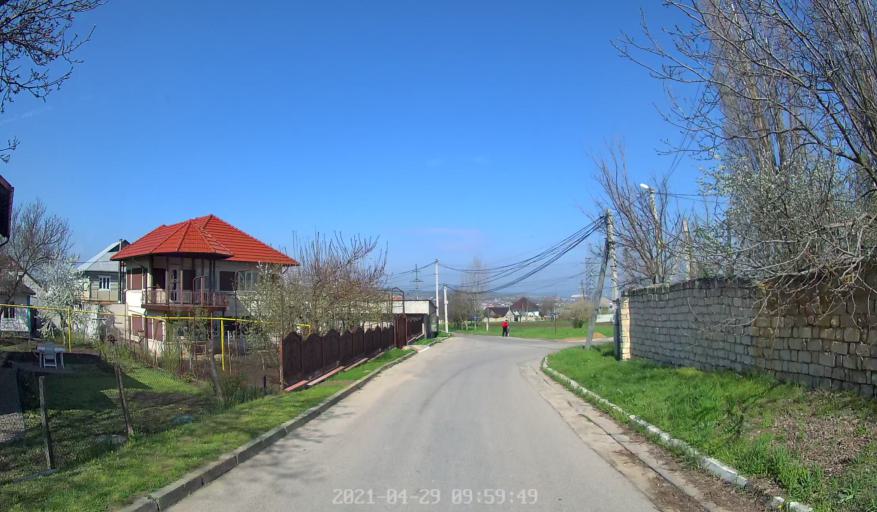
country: MD
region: Chisinau
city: Cricova
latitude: 47.1451
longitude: 28.8551
